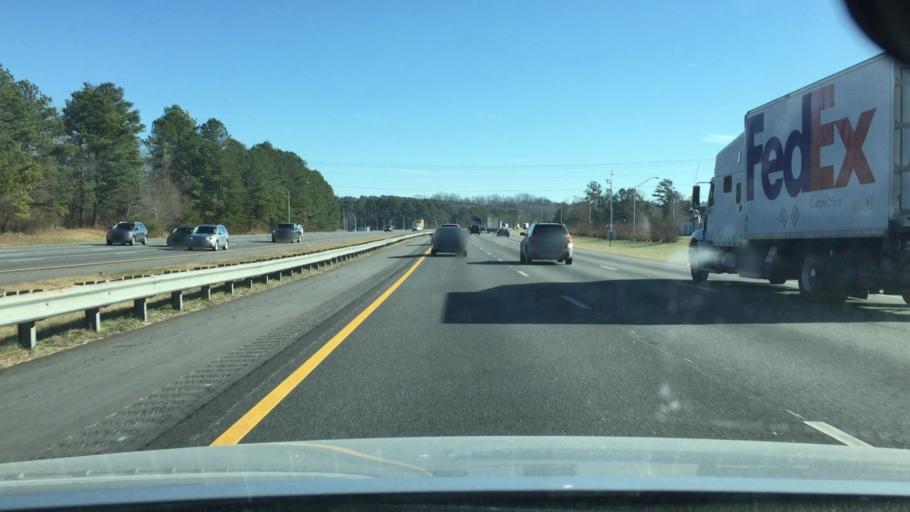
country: US
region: Georgia
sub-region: Catoosa County
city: Ringgold
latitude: 34.8822
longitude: -85.0542
